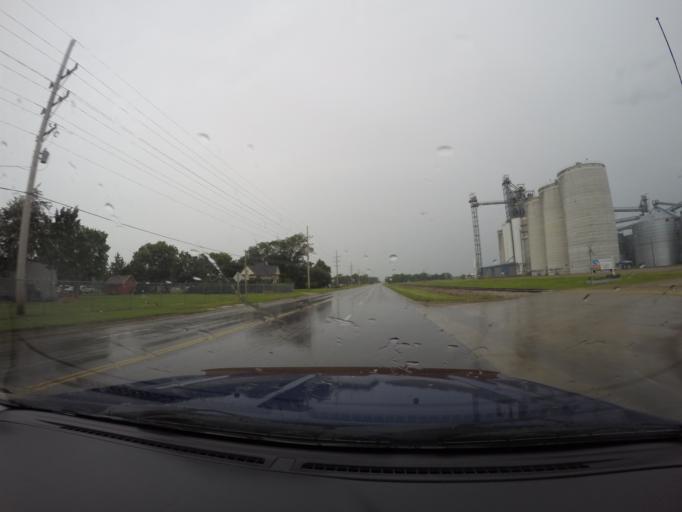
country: US
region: Kansas
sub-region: Cloud County
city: Concordia
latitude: 39.5736
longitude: -97.6752
